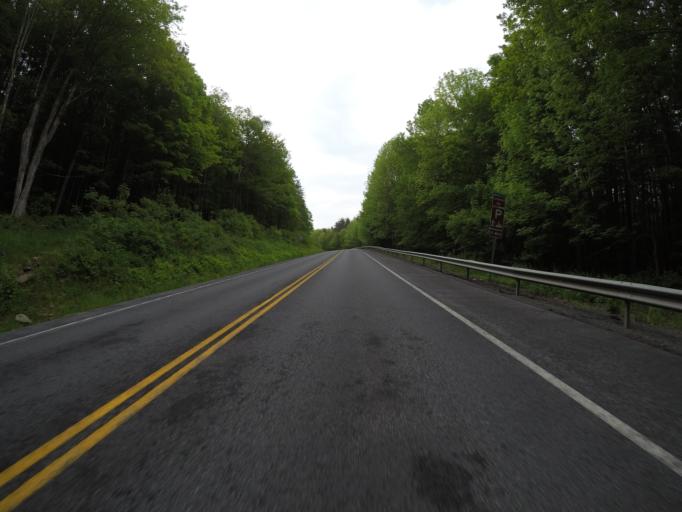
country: US
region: New York
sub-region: Sullivan County
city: Livingston Manor
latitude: 42.0554
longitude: -74.9174
